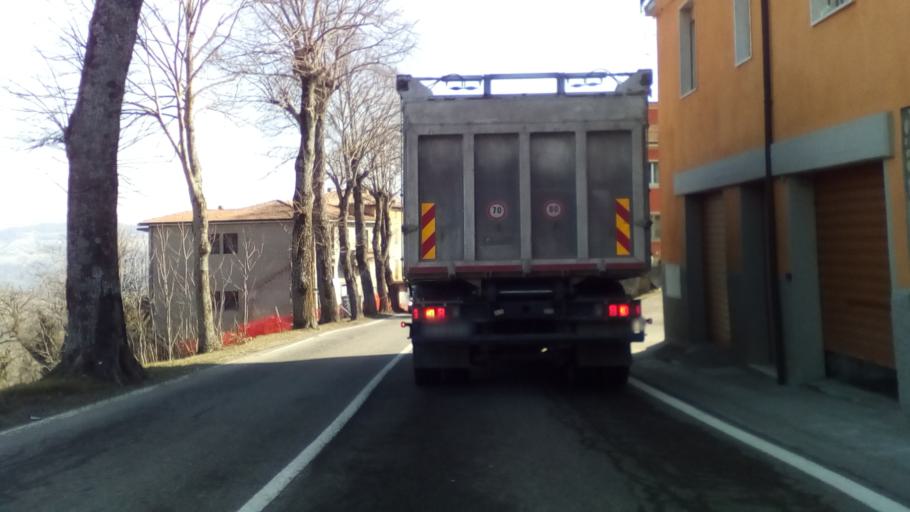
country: IT
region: Emilia-Romagna
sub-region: Provincia di Modena
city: Lama
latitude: 44.3120
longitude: 10.7648
